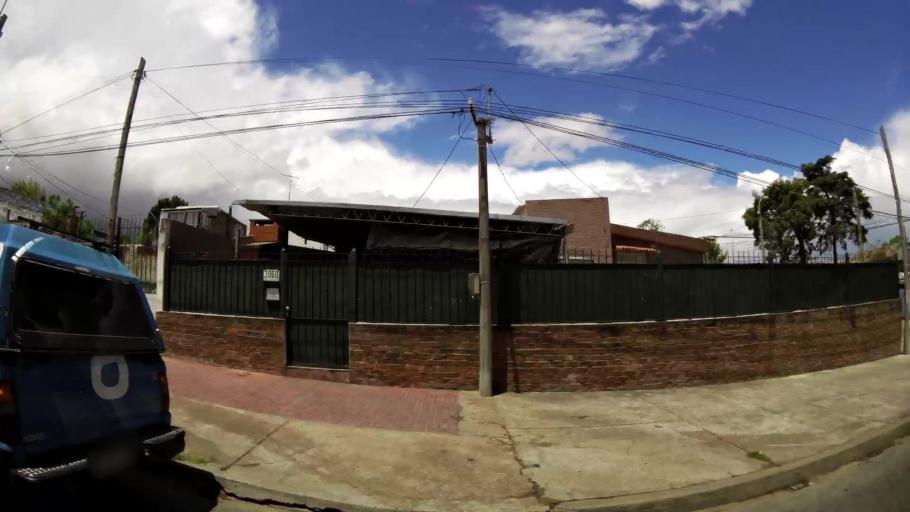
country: UY
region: Montevideo
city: Montevideo
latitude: -34.8506
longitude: -56.1792
